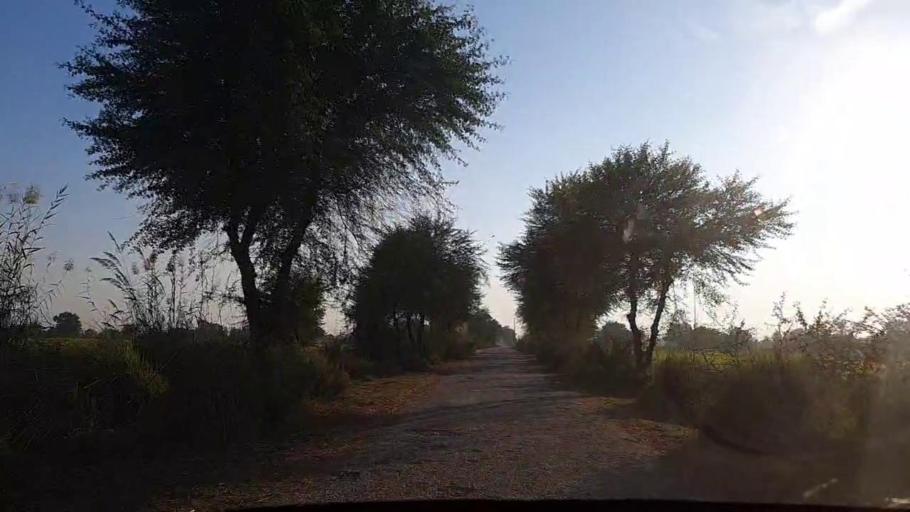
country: PK
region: Sindh
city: Sobhadero
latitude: 27.4019
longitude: 68.3900
